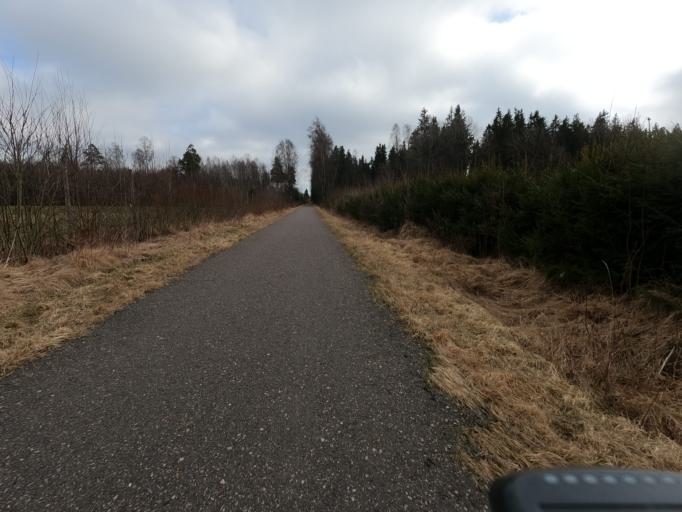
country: SE
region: Joenkoeping
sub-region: Varnamo Kommun
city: Rydaholm
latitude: 56.8603
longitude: 14.1752
